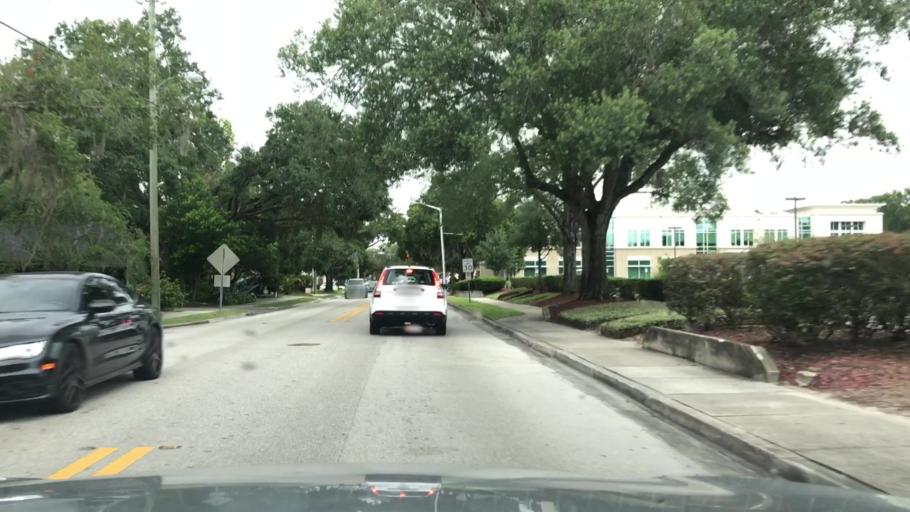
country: US
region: Florida
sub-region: Orange County
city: Winter Park
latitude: 28.5948
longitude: -81.3279
